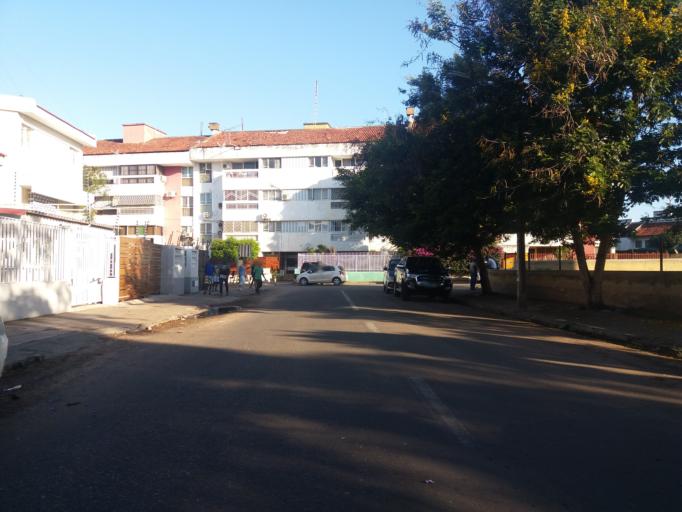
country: MZ
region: Maputo City
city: Maputo
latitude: -25.9511
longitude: 32.5935
